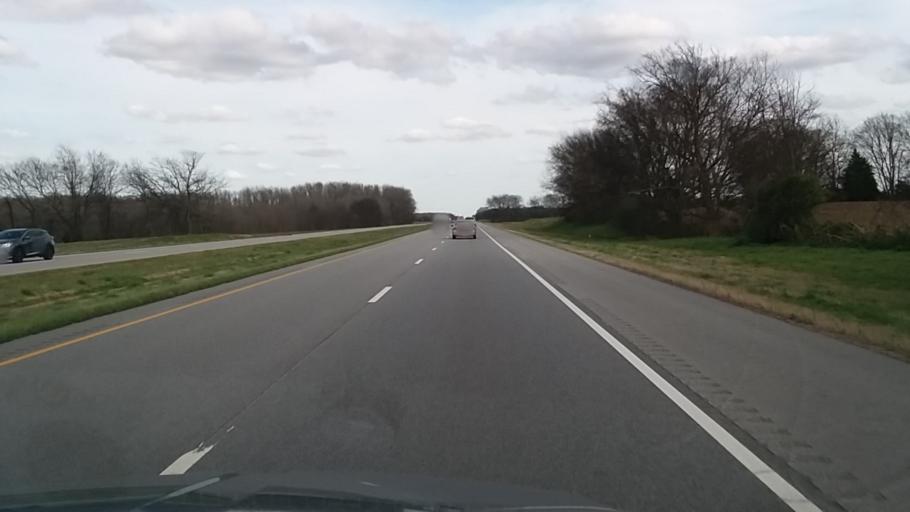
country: US
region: Alabama
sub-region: Lawrence County
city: Town Creek
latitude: 34.6834
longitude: -87.5091
